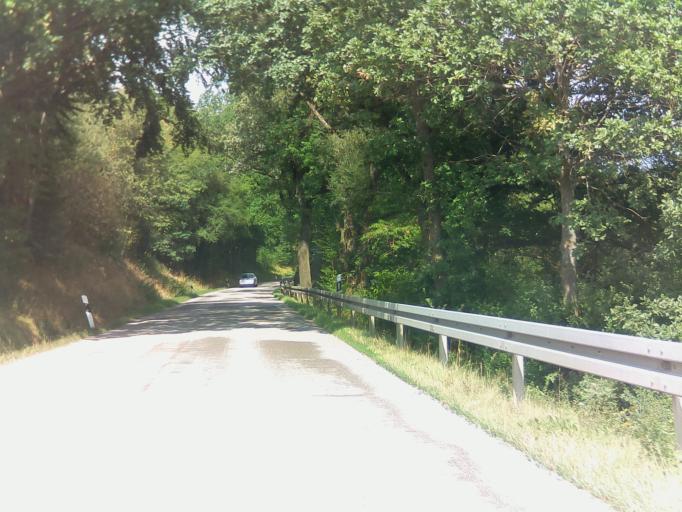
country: DE
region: Hesse
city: Grebenau
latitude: 50.7324
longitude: 9.4695
